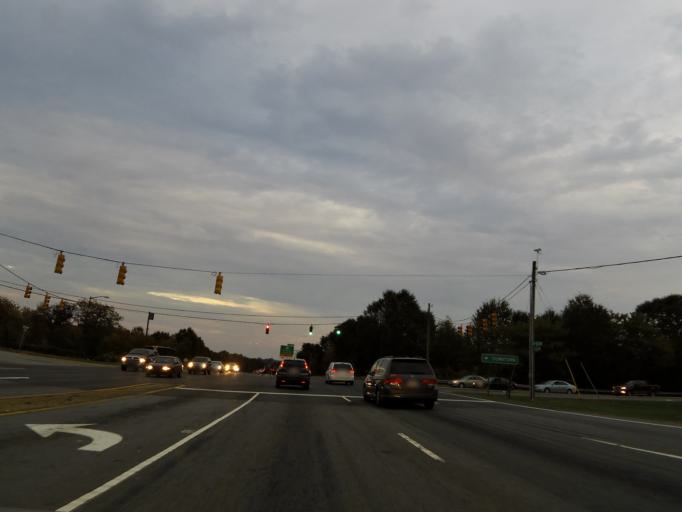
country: US
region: North Carolina
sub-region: Catawba County
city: Longview
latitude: 35.7279
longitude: -81.3621
